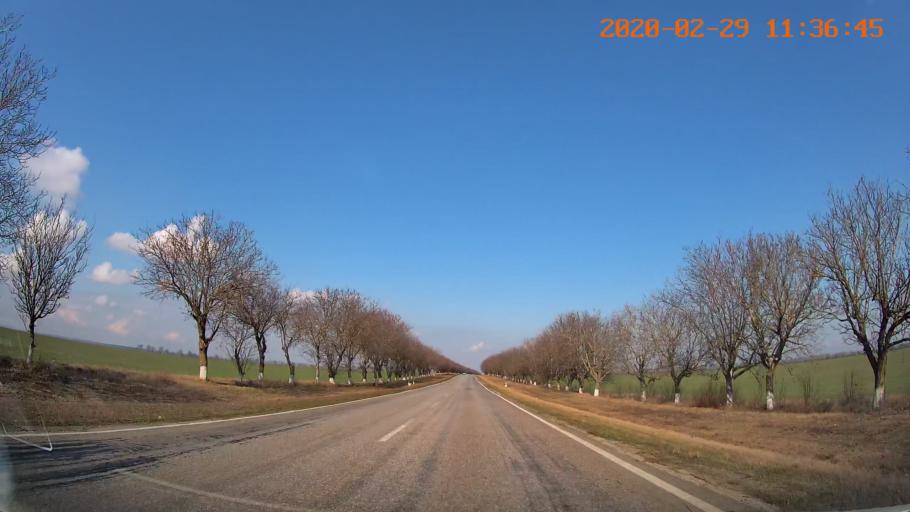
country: MD
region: Rezina
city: Saharna
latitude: 47.6009
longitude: 29.0526
